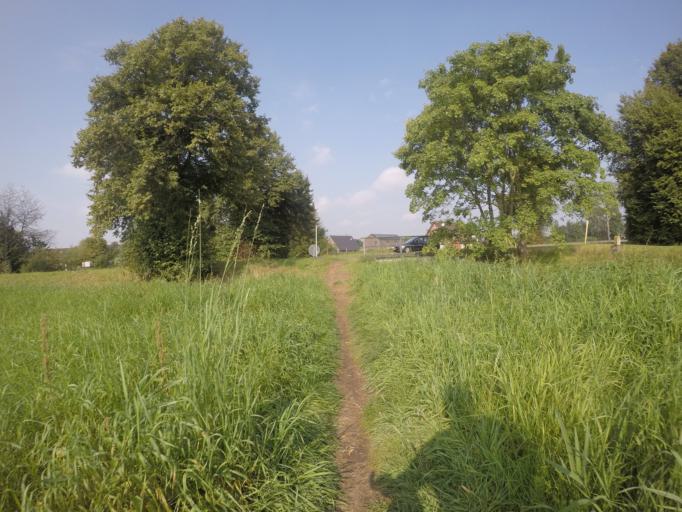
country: DE
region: North Rhine-Westphalia
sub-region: Regierungsbezirk Munster
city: Isselburg
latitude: 51.8210
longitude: 6.5210
